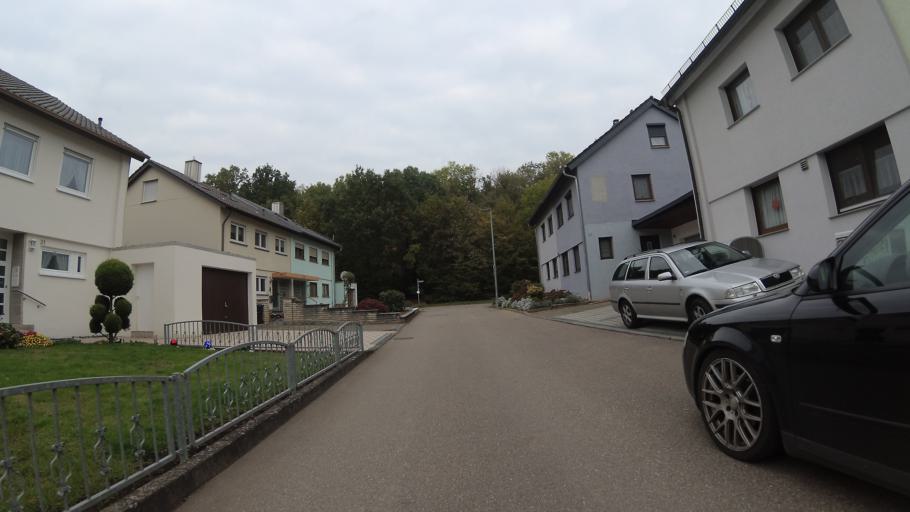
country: DE
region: Baden-Wuerttemberg
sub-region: Regierungsbezirk Stuttgart
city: Untereisesheim
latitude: 49.2305
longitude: 9.2092
